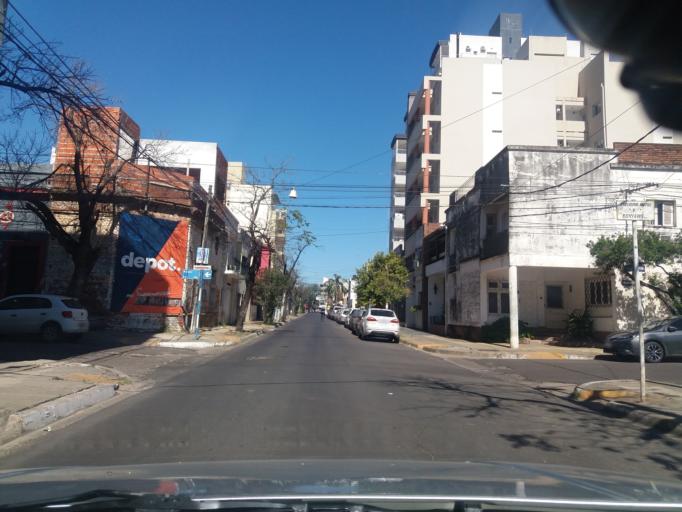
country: AR
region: Corrientes
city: Corrientes
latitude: -27.4729
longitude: -58.8395
